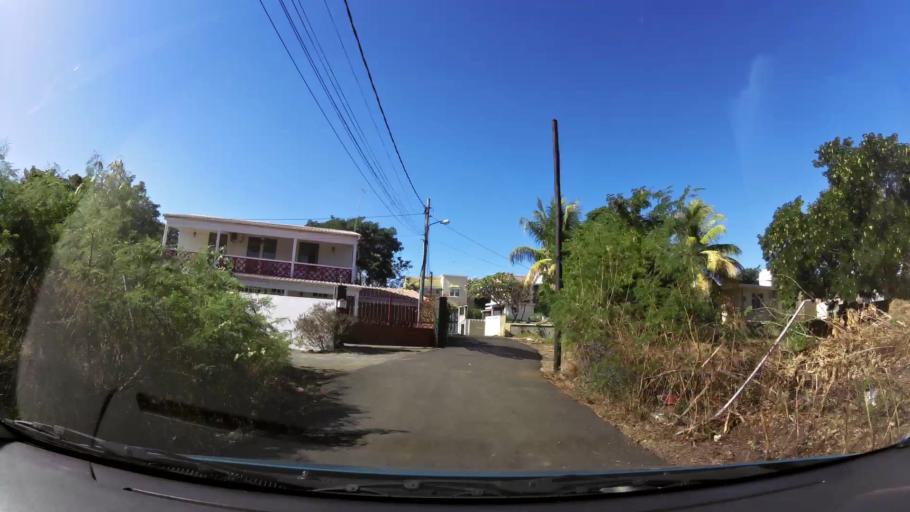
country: MU
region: Black River
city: Flic en Flac
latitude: -20.2624
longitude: 57.3790
